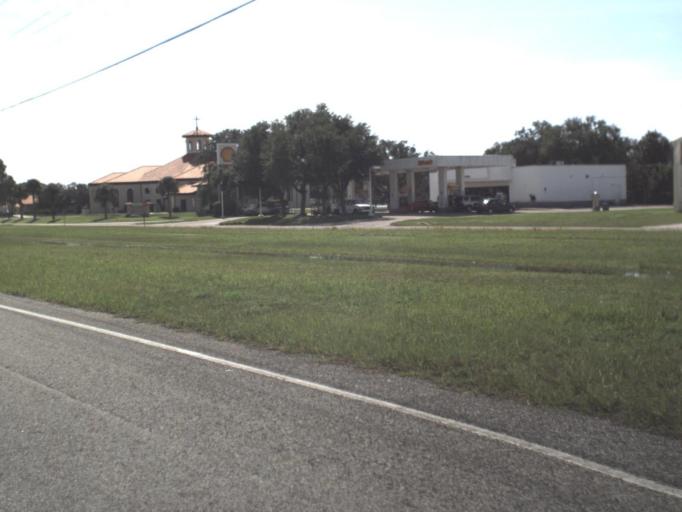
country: US
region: Florida
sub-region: Sarasota County
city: North Port
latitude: 27.0440
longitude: -82.2374
